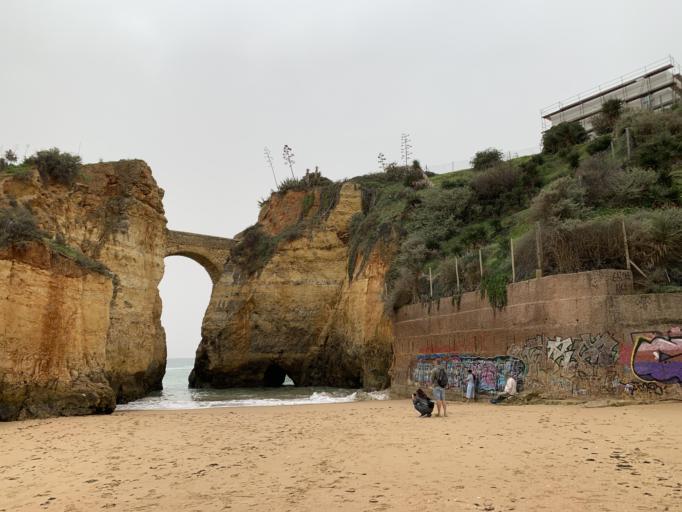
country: PT
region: Faro
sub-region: Lagos
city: Lagos
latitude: 37.0962
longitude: -8.6674
